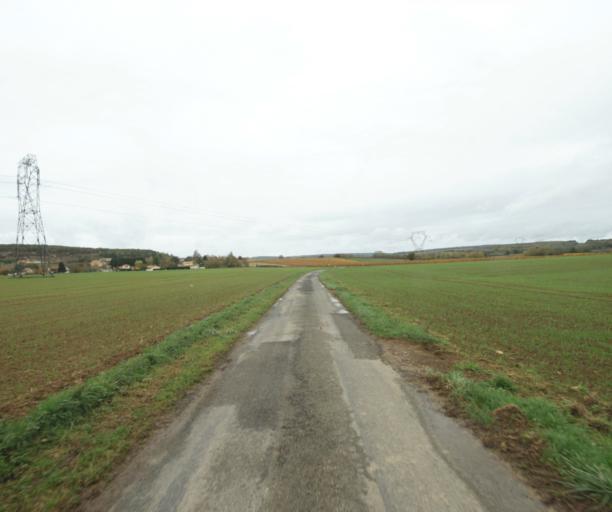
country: FR
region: Bourgogne
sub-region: Departement de Saone-et-Loire
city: Saint-Martin-Belle-Roche
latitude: 46.4684
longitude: 4.8590
